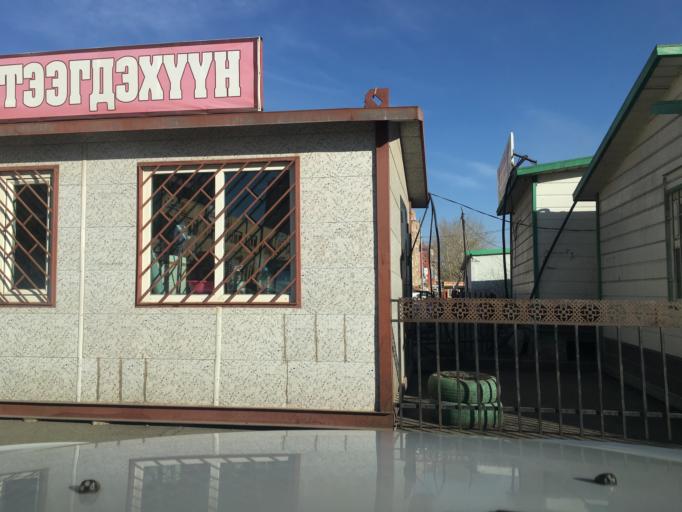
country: MN
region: Ulaanbaatar
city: Ulaanbaatar
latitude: 47.9126
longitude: 106.8454
